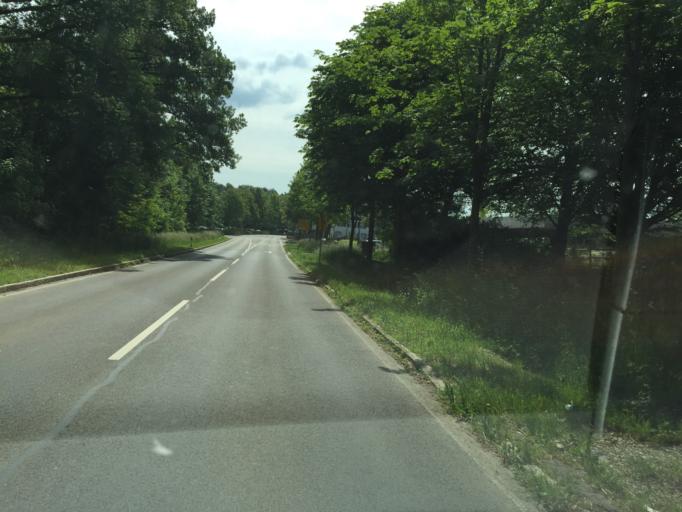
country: DE
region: Baden-Wuerttemberg
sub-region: Regierungsbezirk Stuttgart
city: Esslingen
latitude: 48.7534
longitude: 9.3473
